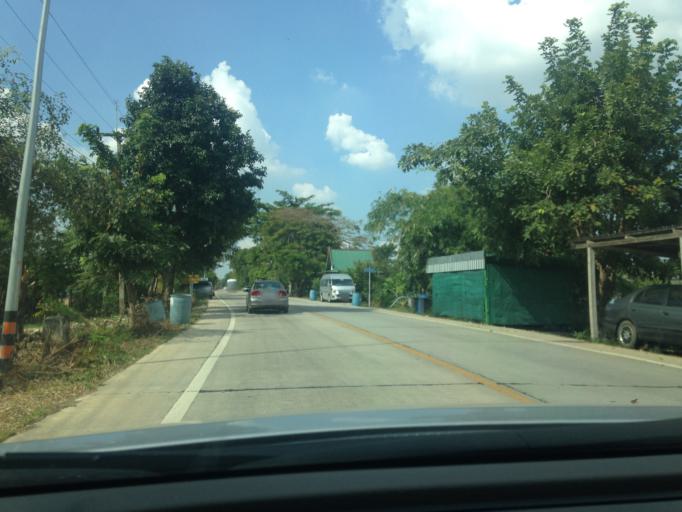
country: TH
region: Pathum Thani
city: Khlong Luang
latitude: 14.0556
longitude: 100.5900
